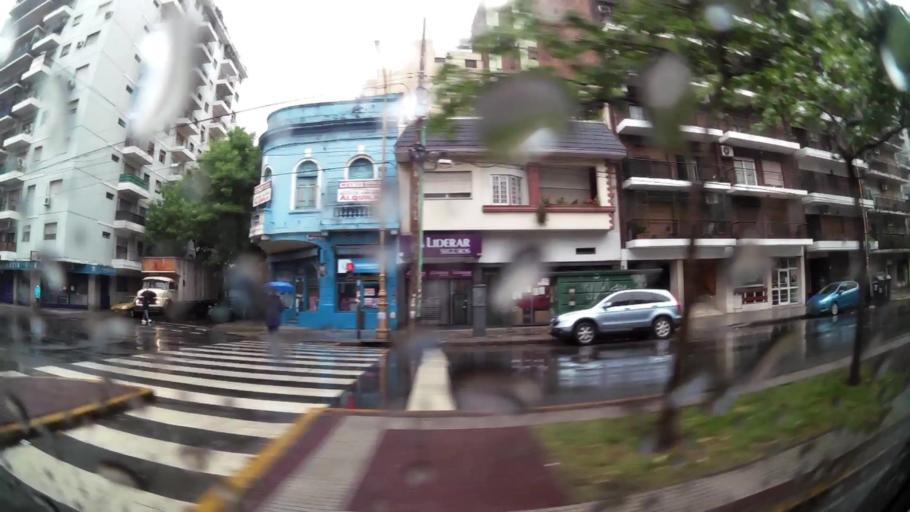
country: AR
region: Buenos Aires
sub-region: Partido de Avellaneda
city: Avellaneda
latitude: -34.6434
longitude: -58.3738
